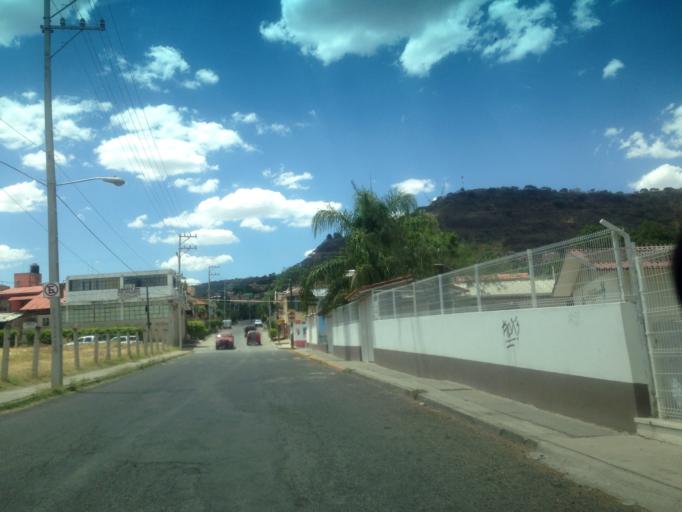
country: MX
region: Jalisco
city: Atotonilco el Alto
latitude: 20.5525
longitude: -102.5009
